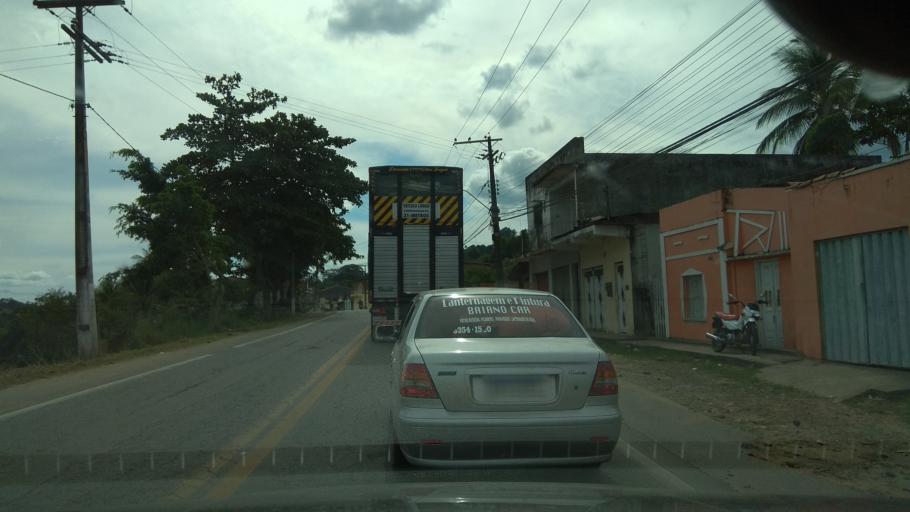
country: BR
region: Bahia
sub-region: Ipiau
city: Ipiau
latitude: -14.1268
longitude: -39.7572
